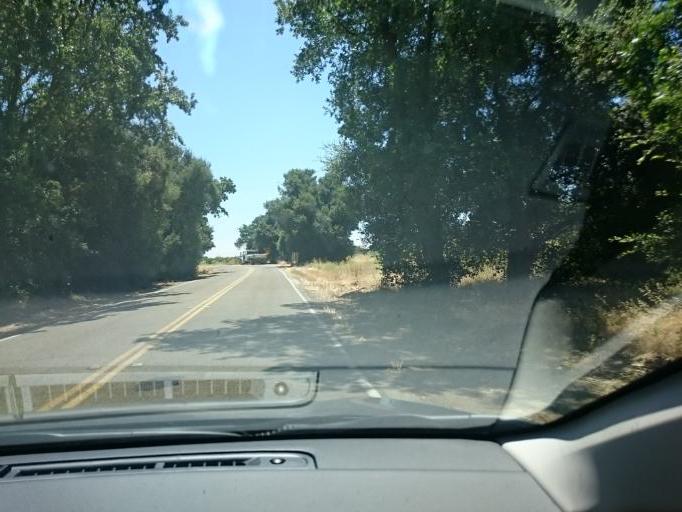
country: US
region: California
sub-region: San Joaquin County
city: Thornton
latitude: 38.2047
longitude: -121.4074
